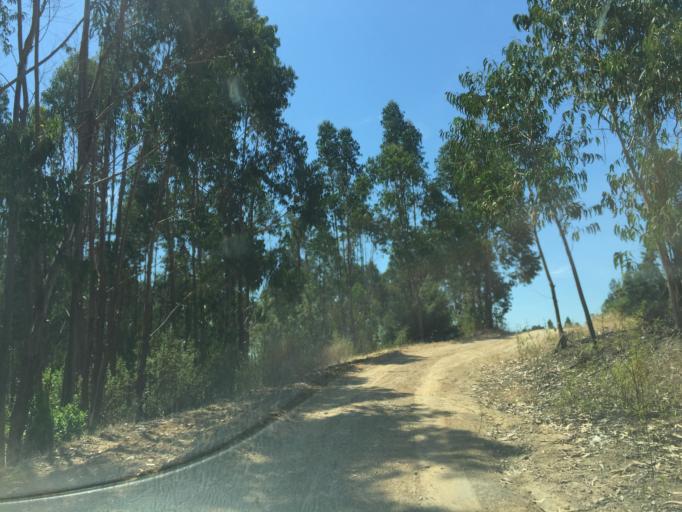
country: PT
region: Santarem
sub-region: Tomar
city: Tomar
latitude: 39.6118
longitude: -8.3613
